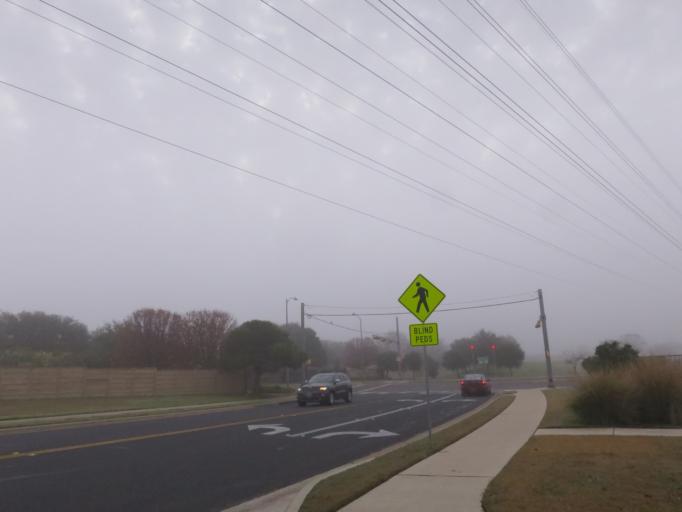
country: US
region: Texas
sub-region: Travis County
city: Wells Branch
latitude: 30.4156
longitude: -97.6887
